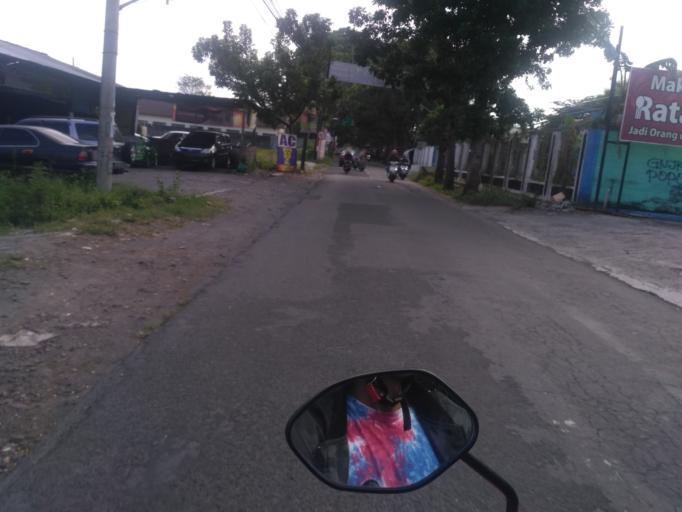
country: ID
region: Daerah Istimewa Yogyakarta
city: Yogyakarta
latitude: -7.7628
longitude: 110.3451
